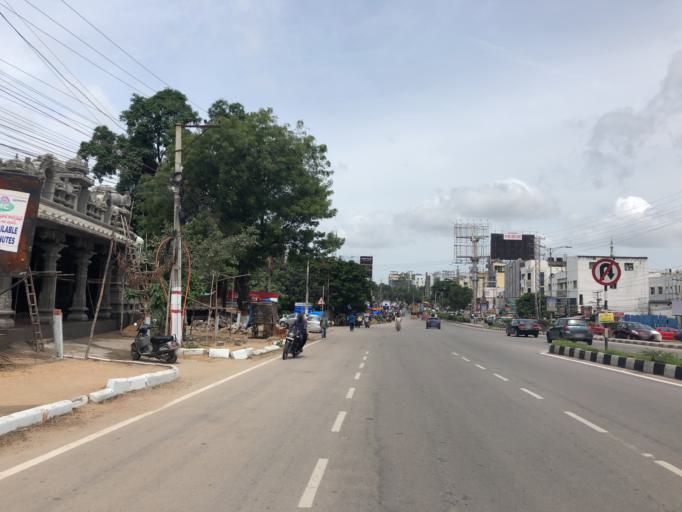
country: IN
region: Telangana
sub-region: Rangareddi
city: Kukatpalli
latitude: 17.4401
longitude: 78.3614
